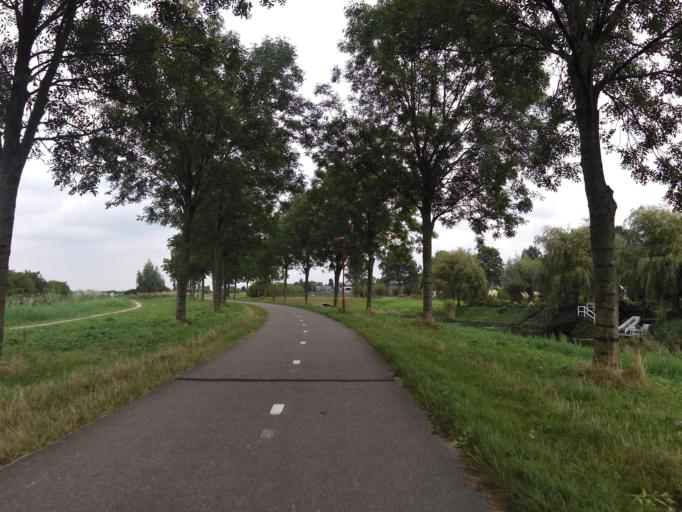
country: NL
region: South Holland
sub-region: Gemeente Rijnwoude
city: Benthuizen
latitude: 52.0746
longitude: 4.5328
